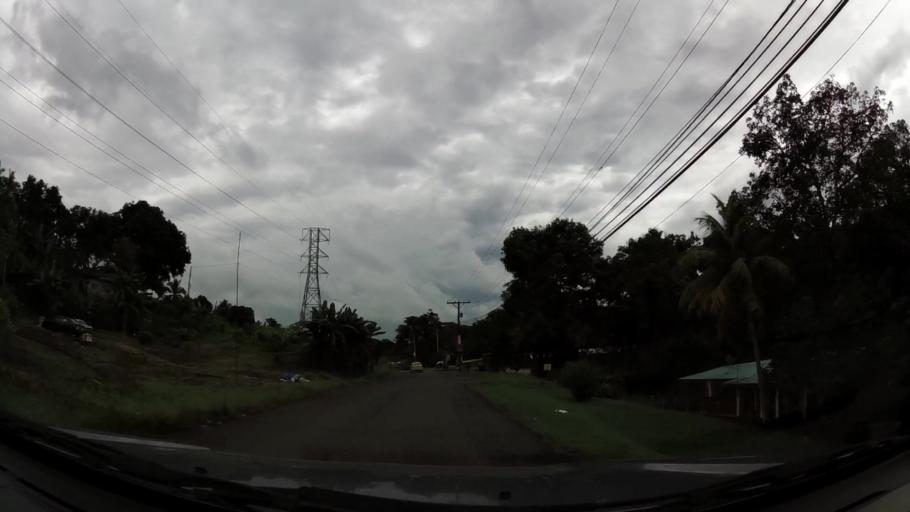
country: PA
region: Panama
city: Chilibre
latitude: 9.1691
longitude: -79.6119
